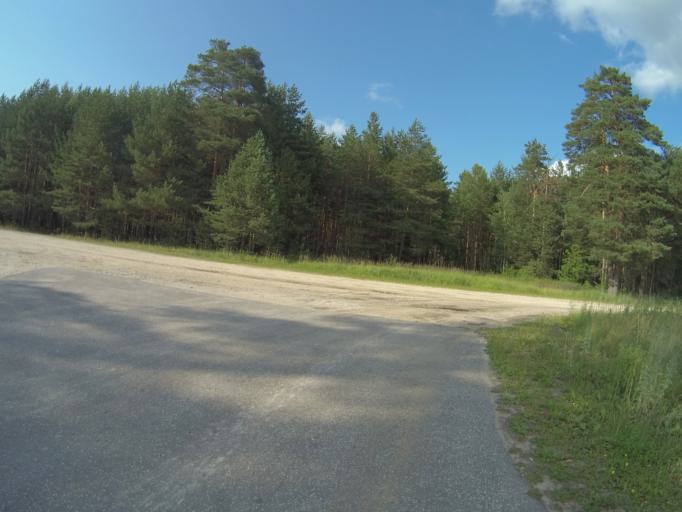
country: RU
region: Vladimir
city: Orgtrud
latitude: 56.3215
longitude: 40.7269
